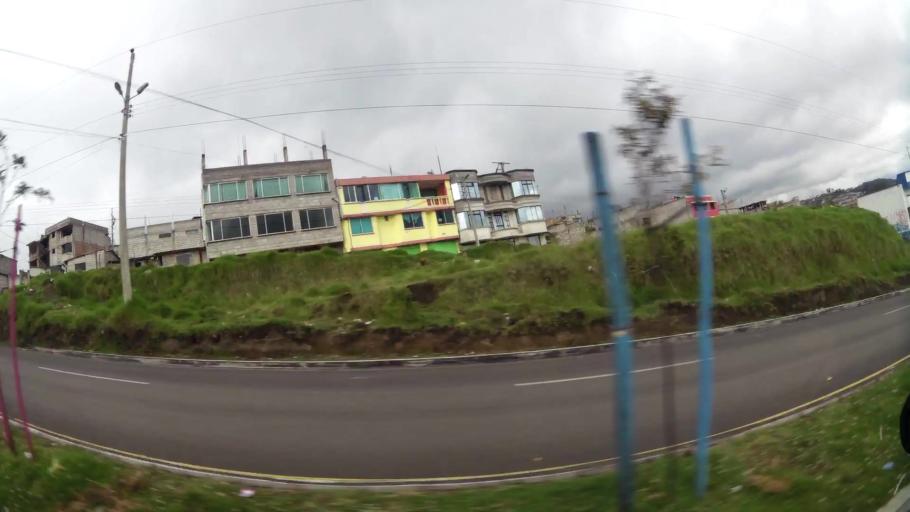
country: EC
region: Pichincha
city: Sangolqui
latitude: -0.3129
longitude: -78.5274
